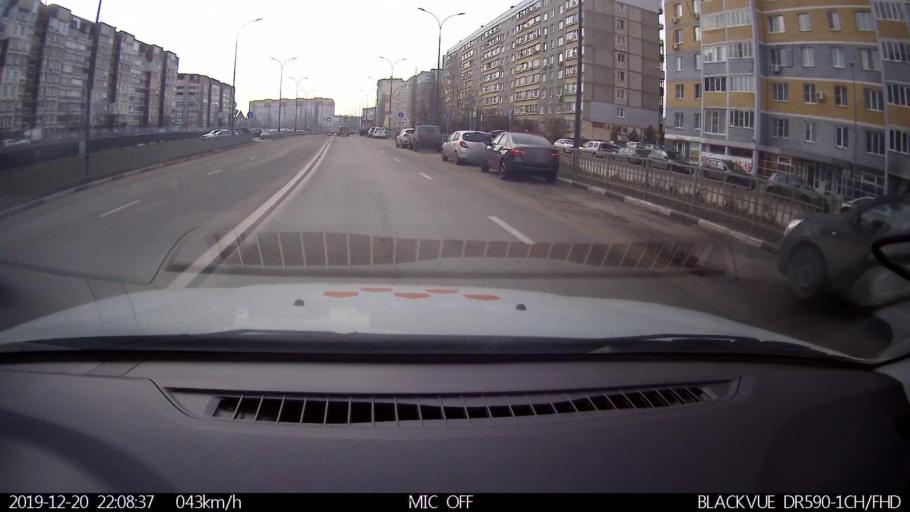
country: RU
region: Nizjnij Novgorod
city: Nizhniy Novgorod
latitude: 56.3468
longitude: 43.9366
